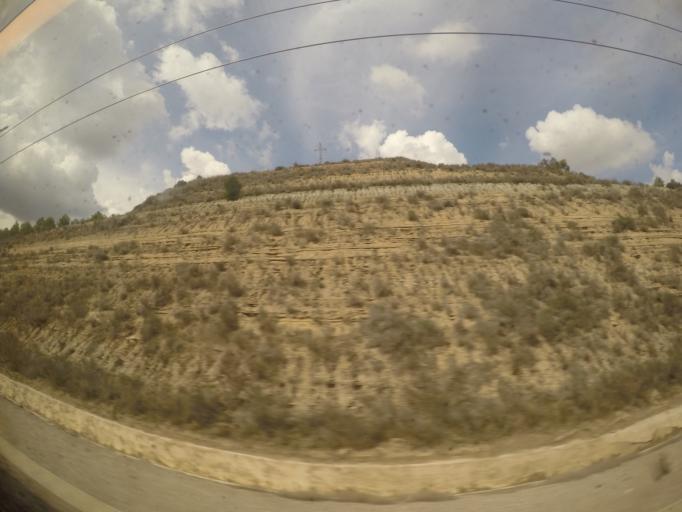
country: ES
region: Catalonia
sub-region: Provincia de Barcelona
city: Sant Llorenc d'Hortons
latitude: 41.4532
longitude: 1.8458
